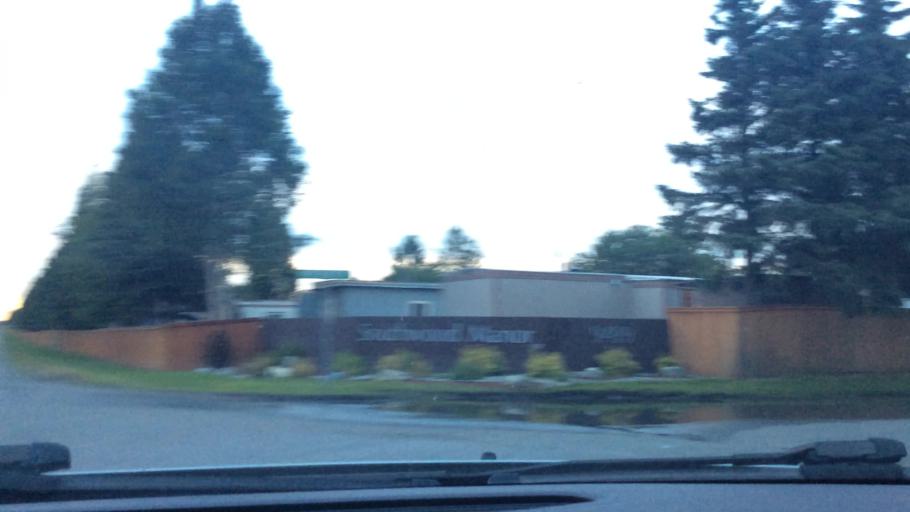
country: US
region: Alaska
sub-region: Anchorage Municipality
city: Anchorage
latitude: 61.1335
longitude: -149.8556
